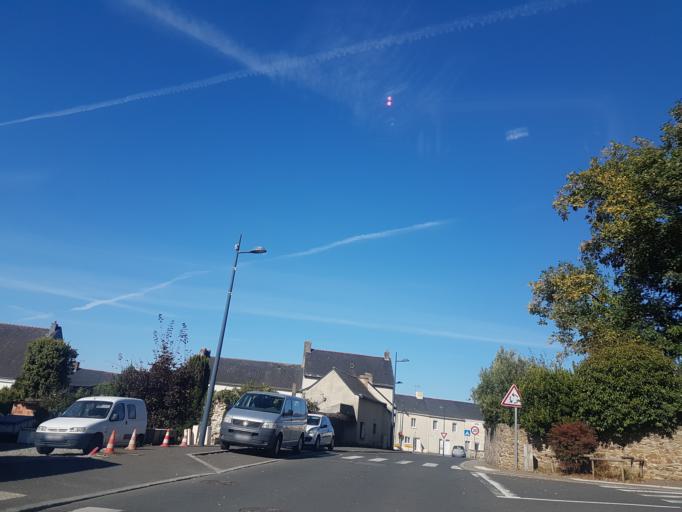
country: FR
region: Pays de la Loire
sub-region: Departement de la Loire-Atlantique
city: Petit-Mars
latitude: 47.3938
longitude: -1.4539
